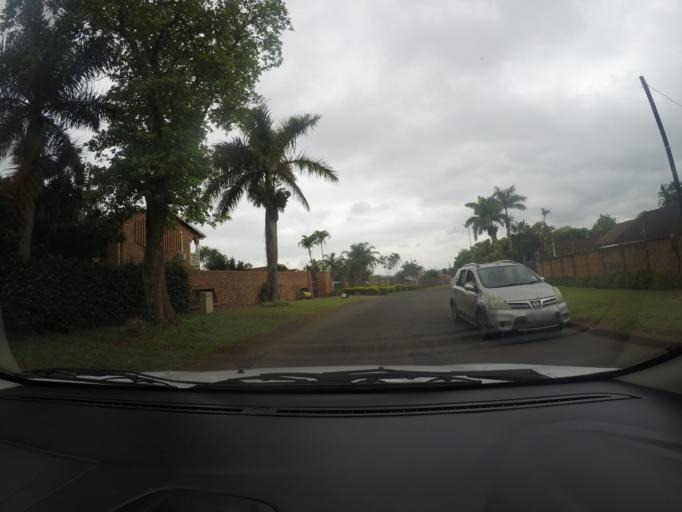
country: ZA
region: KwaZulu-Natal
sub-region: uThungulu District Municipality
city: Empangeni
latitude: -28.7646
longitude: 31.8913
